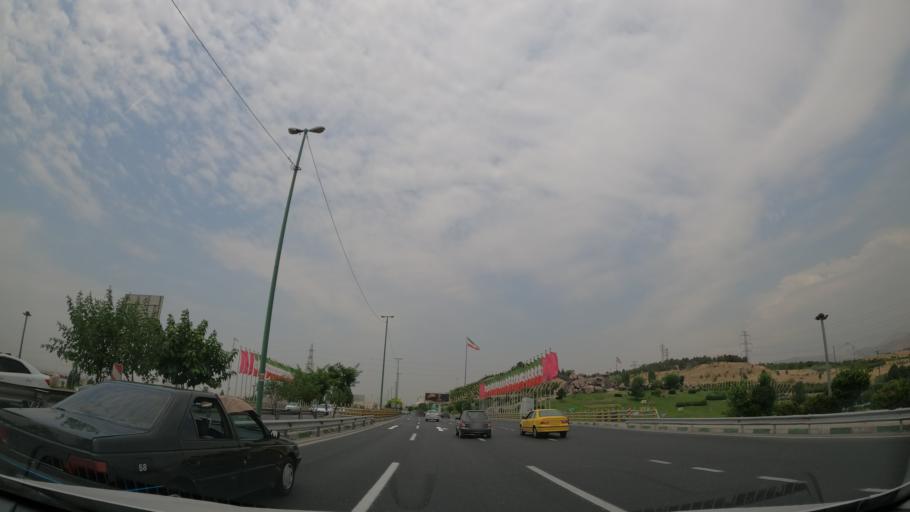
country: IR
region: Tehran
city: Tehran
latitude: 35.7409
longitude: 51.3477
